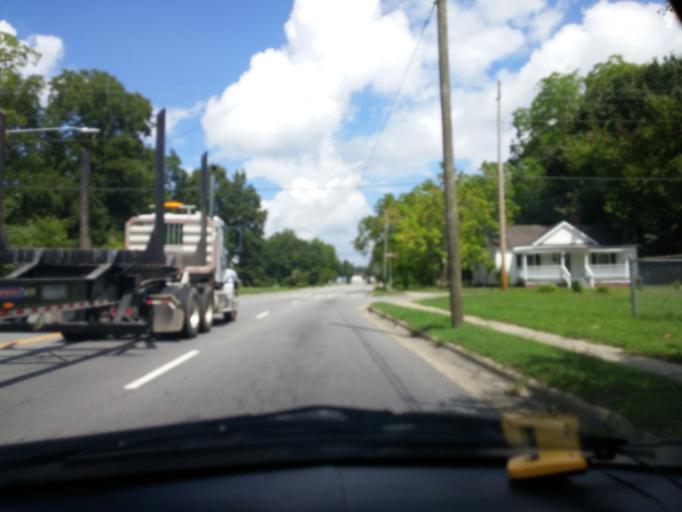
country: US
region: North Carolina
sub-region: Lenoir County
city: Kinston
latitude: 35.2623
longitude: -77.5726
